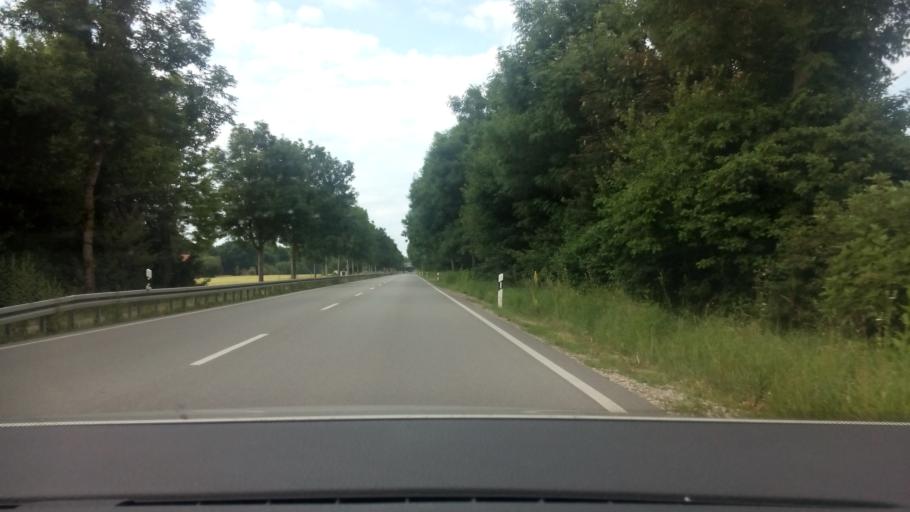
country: DE
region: Bavaria
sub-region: Upper Bavaria
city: Garching bei Munchen
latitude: 48.2243
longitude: 11.6391
